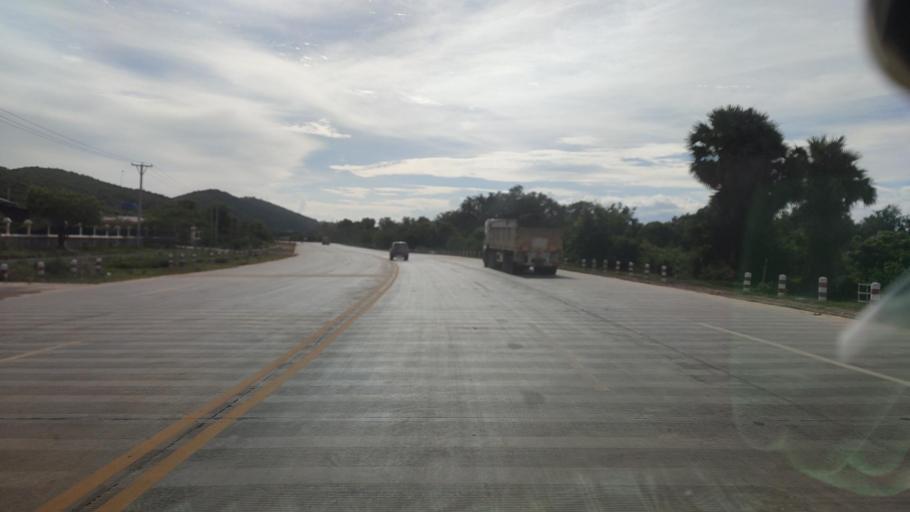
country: MM
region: Mandalay
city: Kyaukse
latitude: 21.6102
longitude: 96.1773
